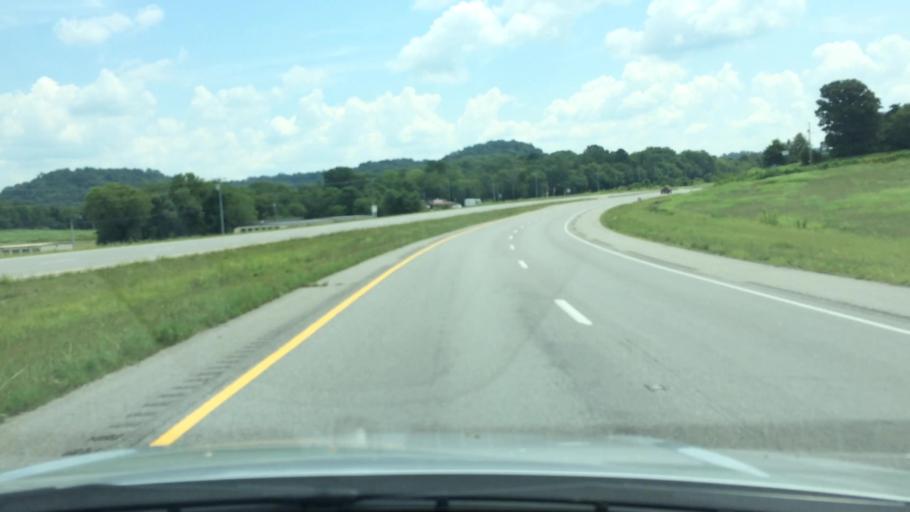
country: US
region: Tennessee
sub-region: Giles County
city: Pulaski
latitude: 35.1813
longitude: -86.9388
